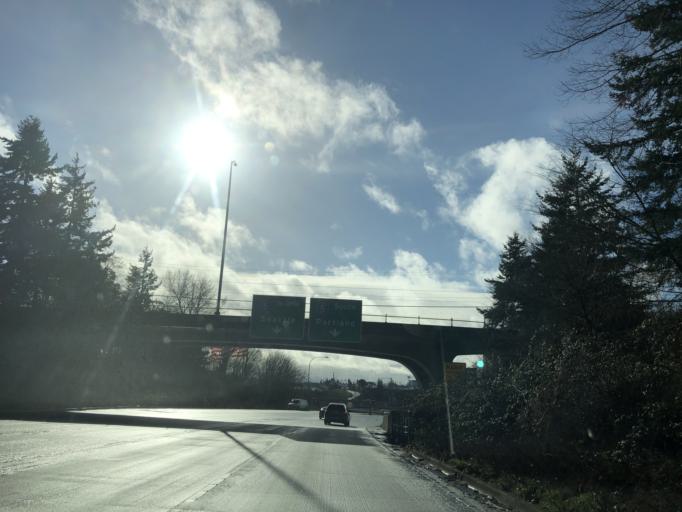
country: US
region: Washington
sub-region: Pierce County
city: Tacoma
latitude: 47.2372
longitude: -122.4633
